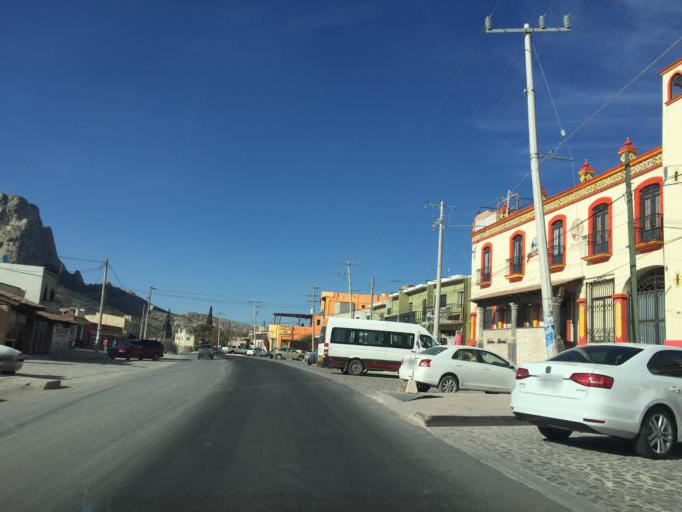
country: MX
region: Queretaro
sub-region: Ezequiel Montes
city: San Jose del Jagueey
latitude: 20.7351
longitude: -99.9373
